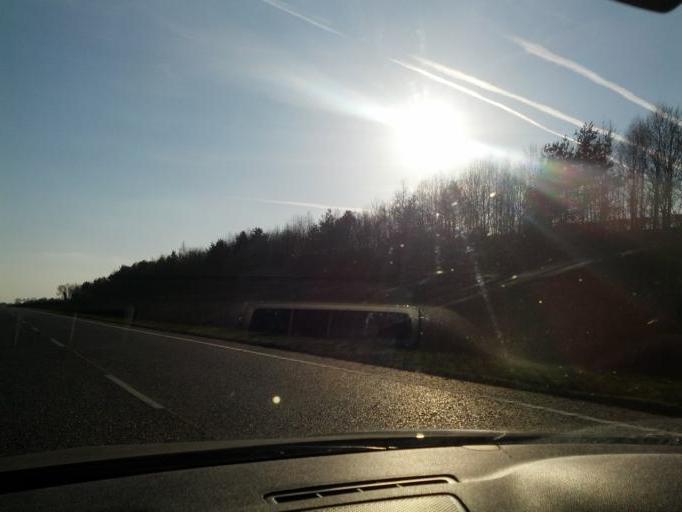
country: IE
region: Leinster
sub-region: Laois
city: Portlaoise
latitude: 53.0301
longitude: -7.2511
